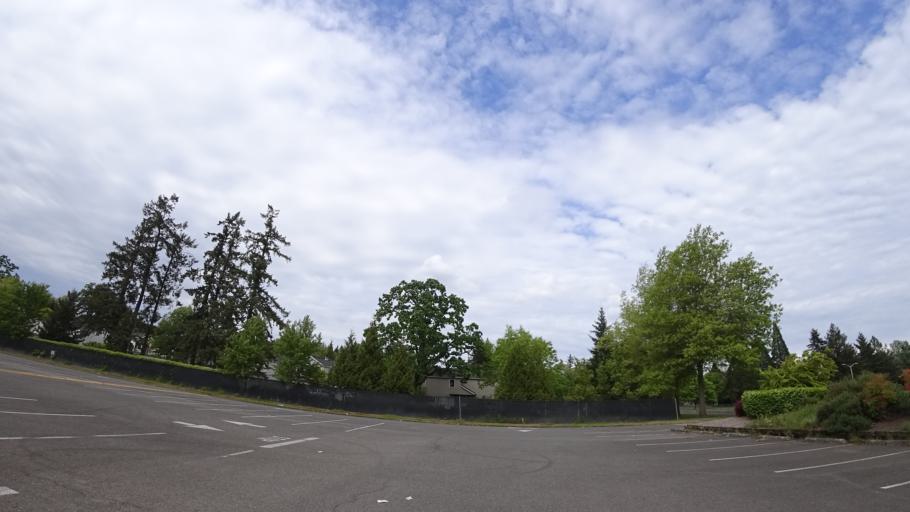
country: US
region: Oregon
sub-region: Washington County
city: Hillsboro
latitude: 45.4954
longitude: -122.9568
